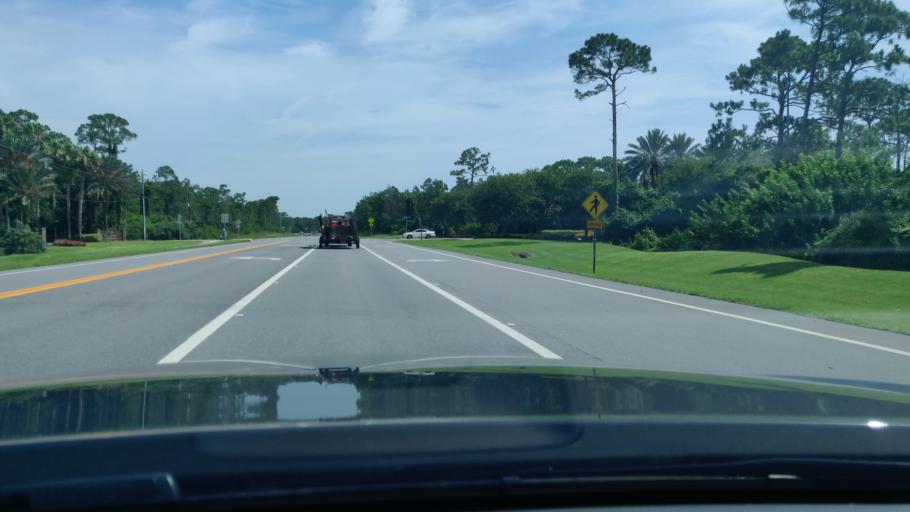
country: US
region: Florida
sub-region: Flagler County
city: Flagler Beach
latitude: 29.5263
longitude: -81.1704
